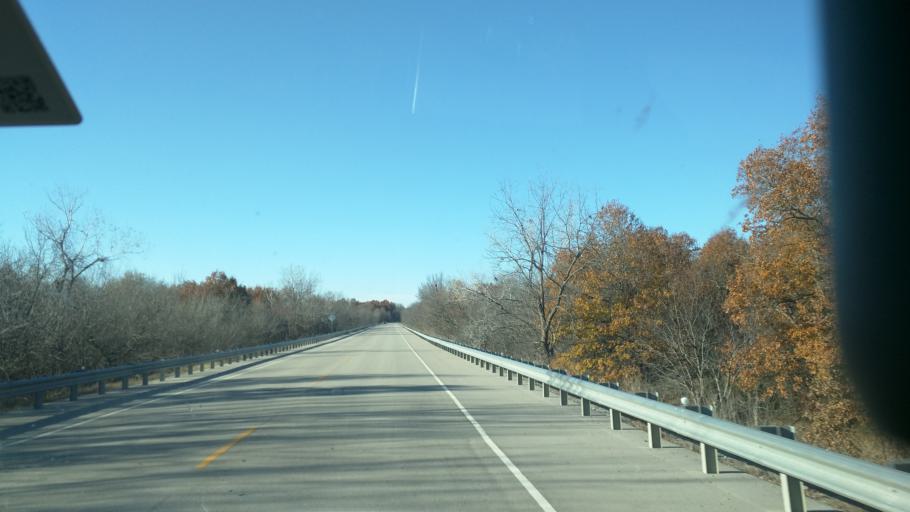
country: US
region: Oklahoma
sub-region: Nowata County
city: Nowata
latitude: 36.7492
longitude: -95.5316
